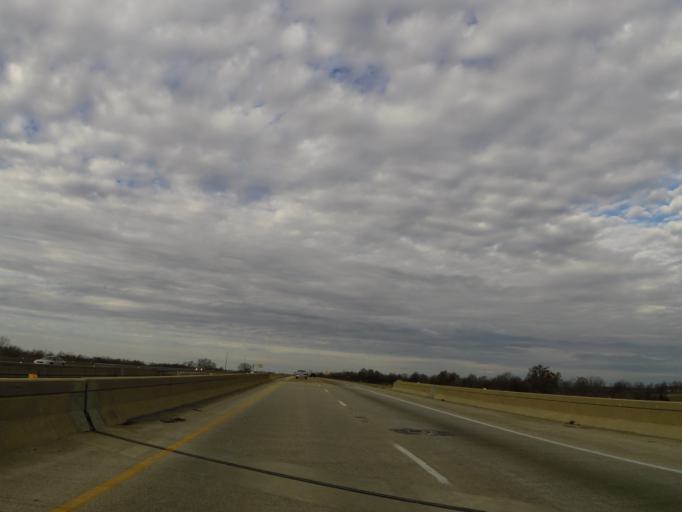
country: US
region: Illinois
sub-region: Clinton County
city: Wamac
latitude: 38.3895
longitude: -89.1698
